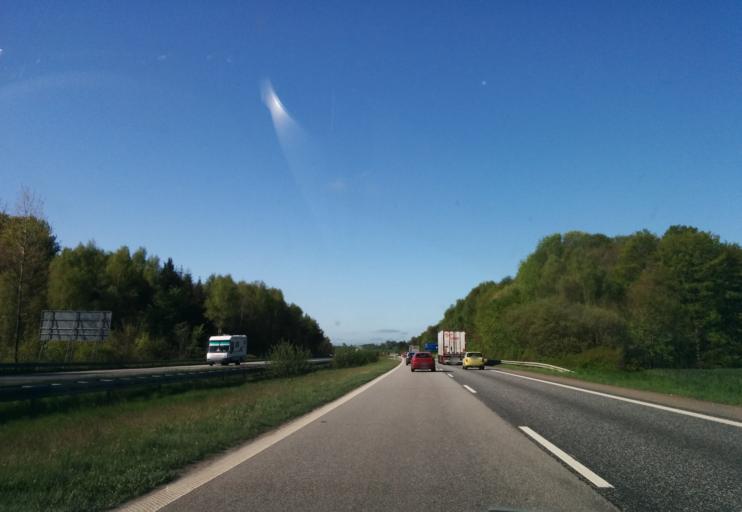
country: DK
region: Central Jutland
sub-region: Skanderborg Kommune
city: Skanderborg
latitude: 56.0392
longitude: 9.8908
